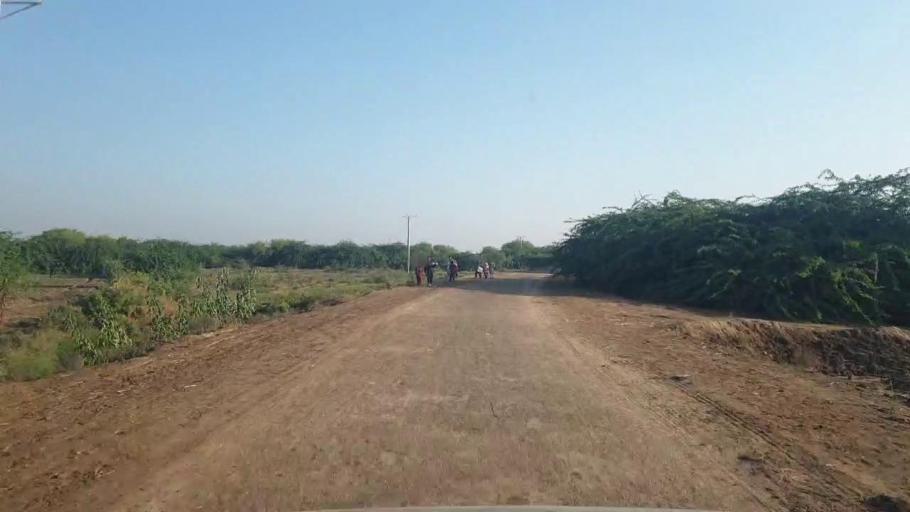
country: PK
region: Sindh
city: Badin
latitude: 24.7139
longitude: 68.8560
